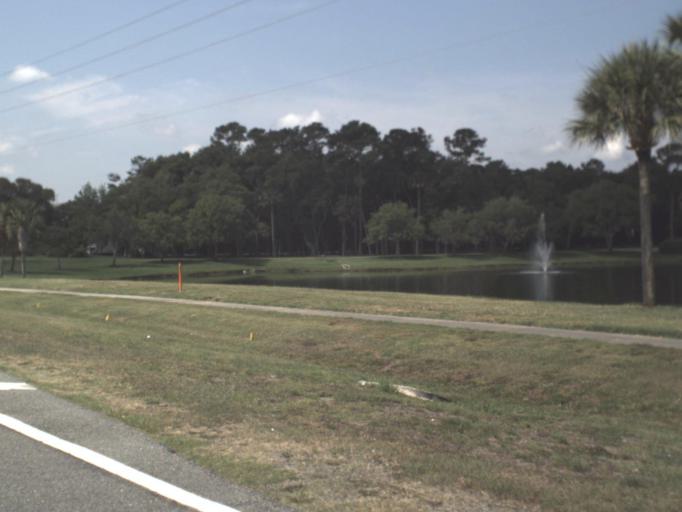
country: US
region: Florida
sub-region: Saint Johns County
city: Sawgrass
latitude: 30.2042
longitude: -81.3802
